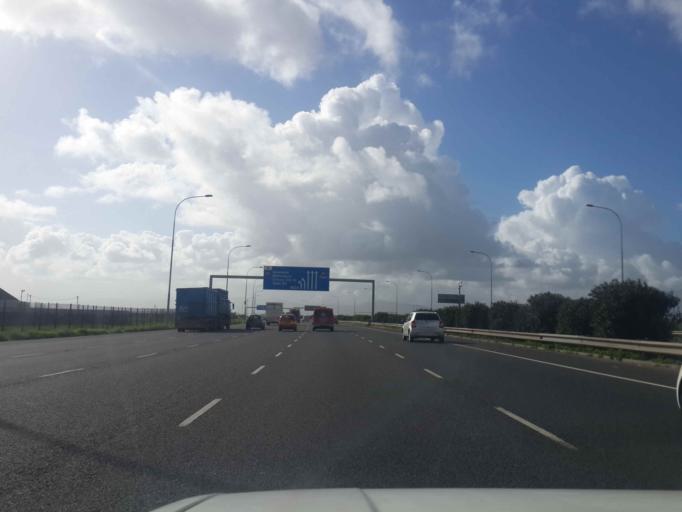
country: ZA
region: Western Cape
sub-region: City of Cape Town
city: Rosebank
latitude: -33.9146
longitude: 18.4929
